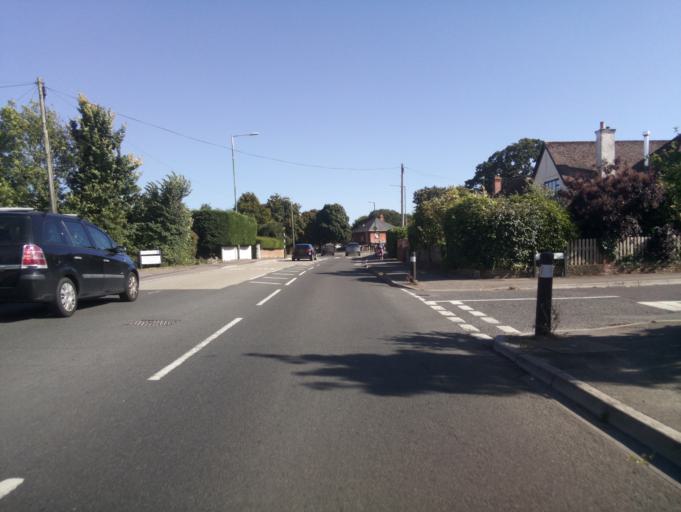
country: GB
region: England
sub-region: Dorset
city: Ferndown
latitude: 50.7700
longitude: -1.8856
